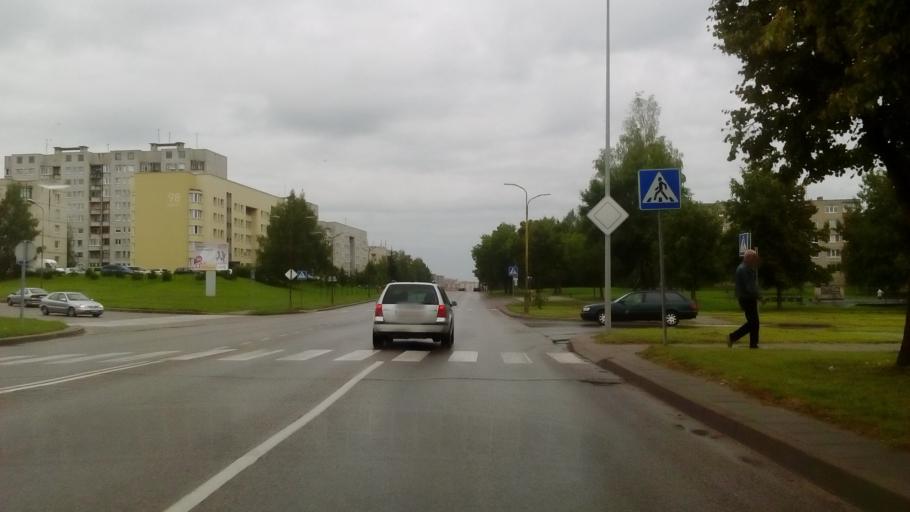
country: LT
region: Alytaus apskritis
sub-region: Alytus
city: Alytus
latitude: 54.3886
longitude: 24.0249
